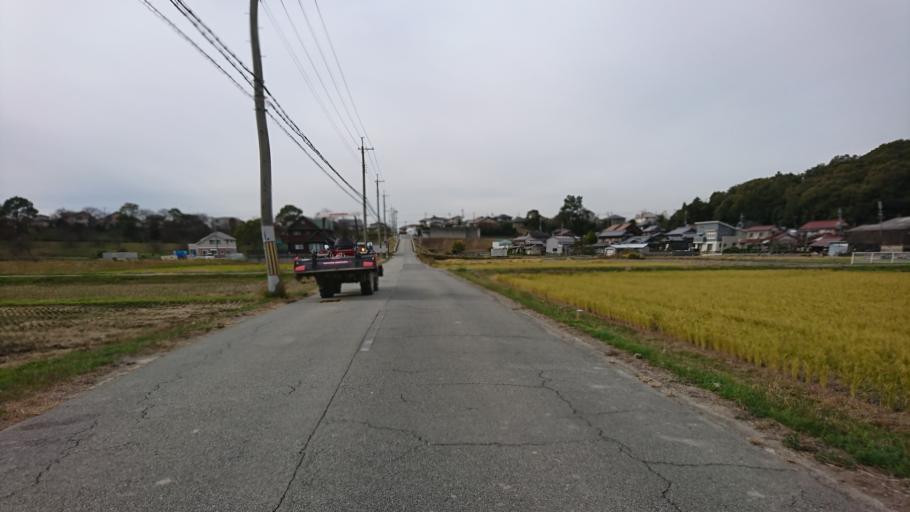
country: JP
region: Hyogo
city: Kakogawacho-honmachi
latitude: 34.7872
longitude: 134.8895
